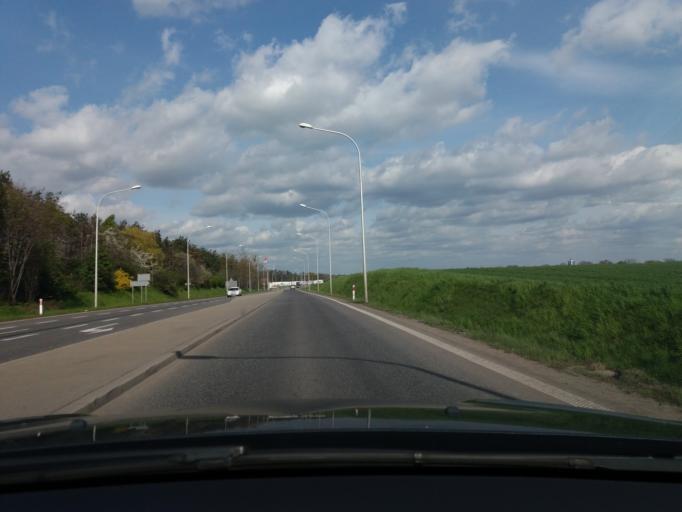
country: PL
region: Lower Silesian Voivodeship
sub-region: Powiat sredzki
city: Sroda Slaska
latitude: 51.1607
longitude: 16.6070
